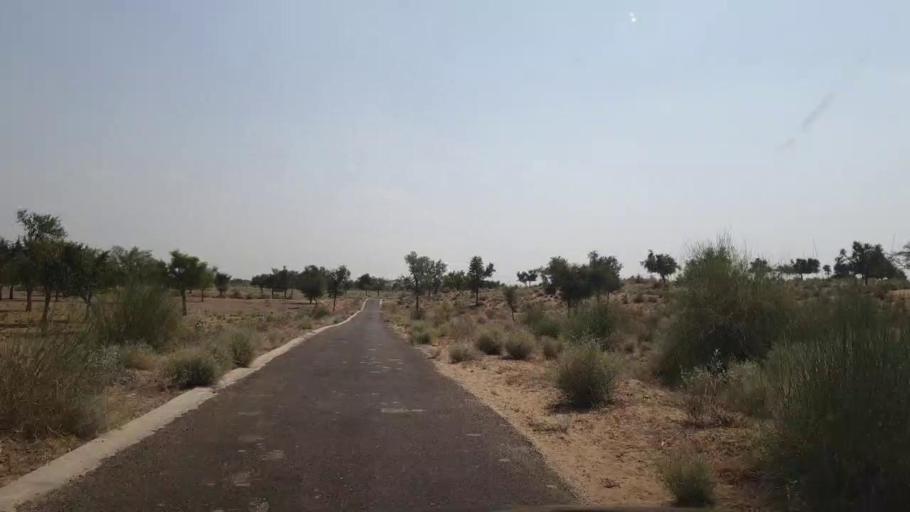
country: PK
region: Sindh
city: Islamkot
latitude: 25.0933
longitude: 70.7314
